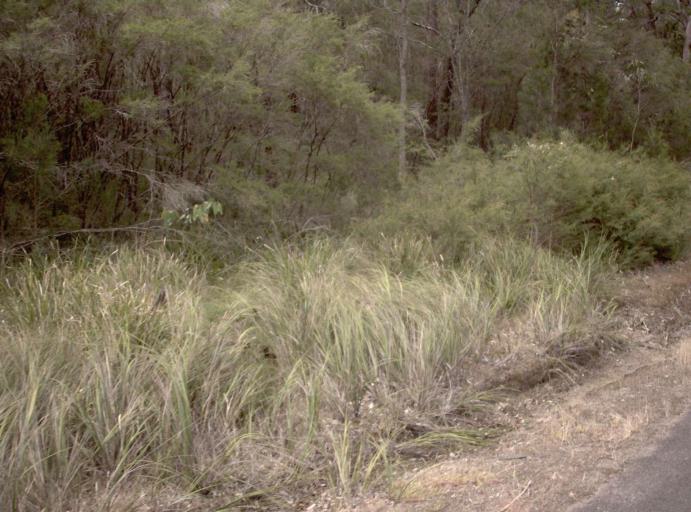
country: AU
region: New South Wales
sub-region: Bega Valley
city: Eden
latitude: -37.4565
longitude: 149.6138
